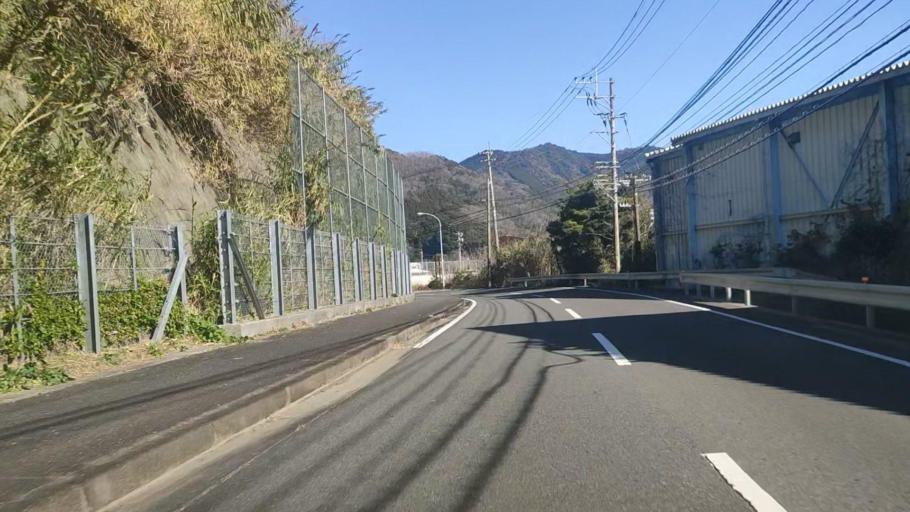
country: JP
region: Oita
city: Saiki
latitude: 32.7994
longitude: 131.9192
